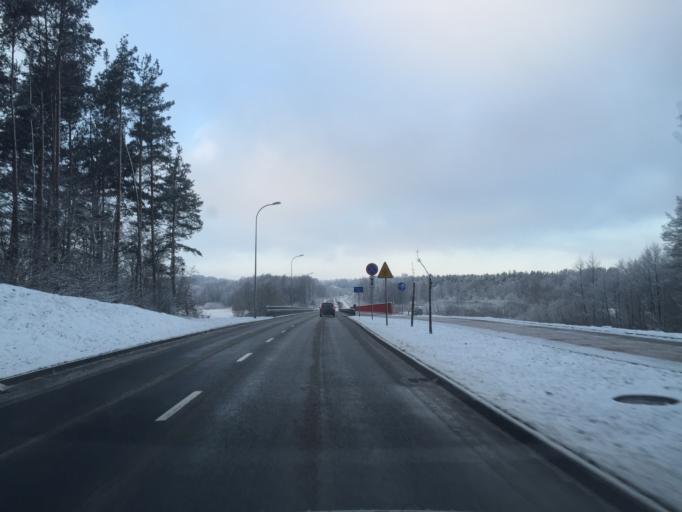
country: PL
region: Kujawsko-Pomorskie
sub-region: Powiat brodnicki
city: Brodnica
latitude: 53.2391
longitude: 19.3827
